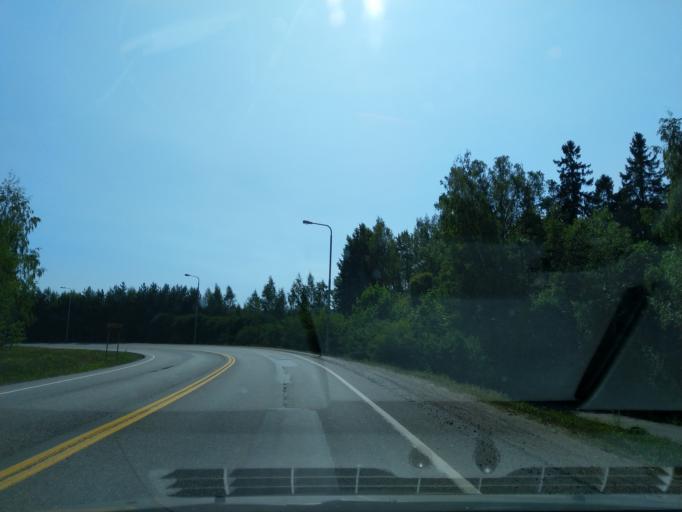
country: FI
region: Uusimaa
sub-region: Helsinki
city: Kilo
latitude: 60.2676
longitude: 24.7621
